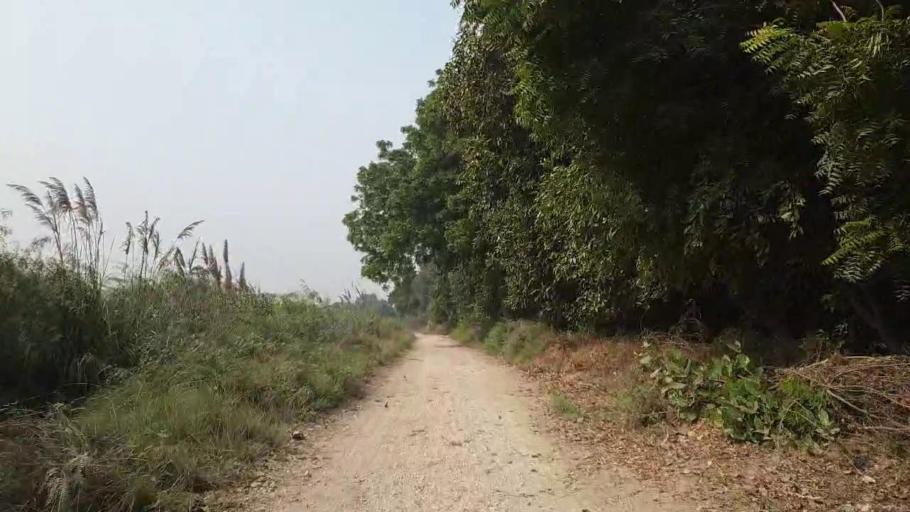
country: PK
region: Sindh
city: Tando Muhammad Khan
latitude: 25.1890
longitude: 68.5941
